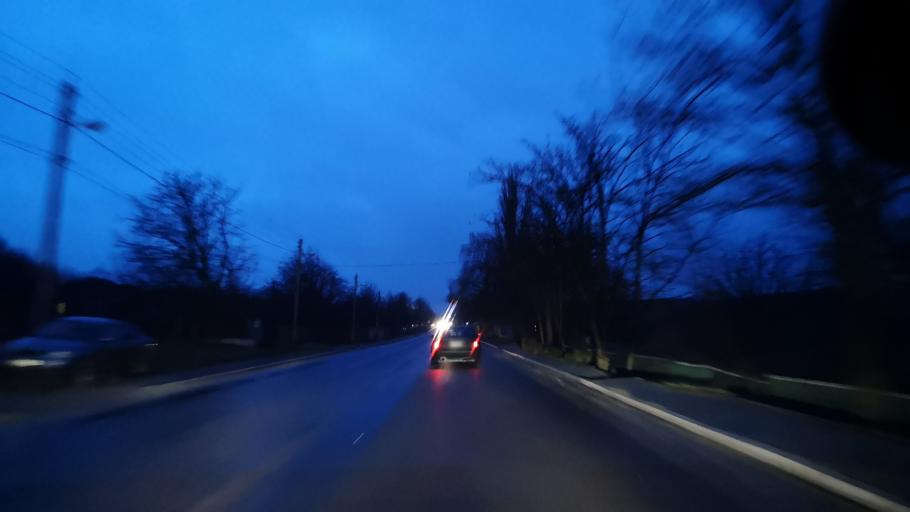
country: MD
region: Orhei
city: Orhei
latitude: 47.4220
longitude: 28.8063
